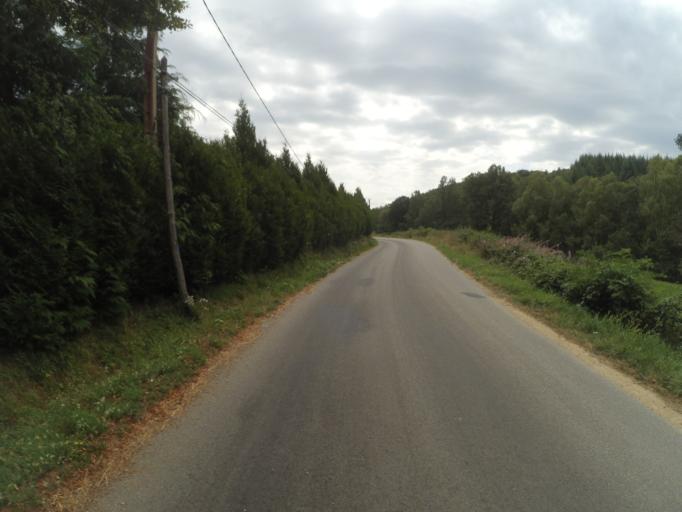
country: FR
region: Limousin
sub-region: Departement de la Creuse
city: La Courtine
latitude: 45.6660
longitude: 2.1649
